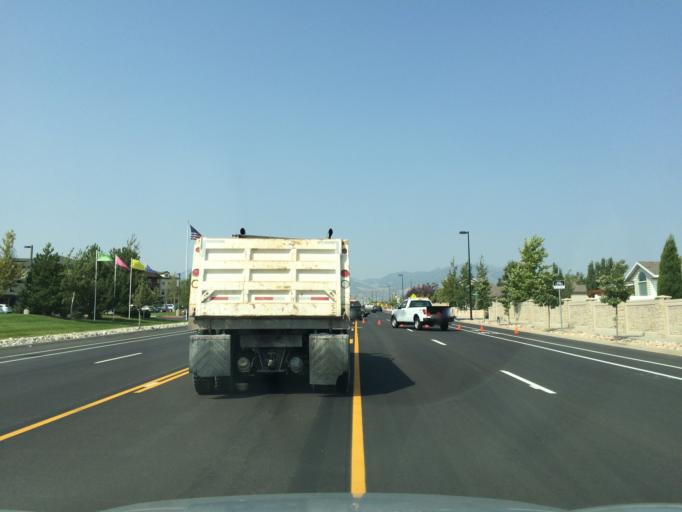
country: US
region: Utah
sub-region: Salt Lake County
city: Oquirrh
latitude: 40.5879
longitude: -112.0205
